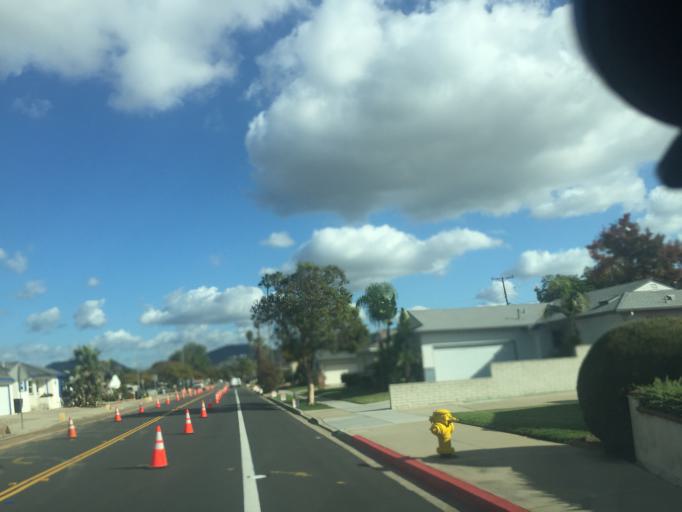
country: US
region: California
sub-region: San Diego County
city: La Mesa
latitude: 32.7946
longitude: -117.0799
